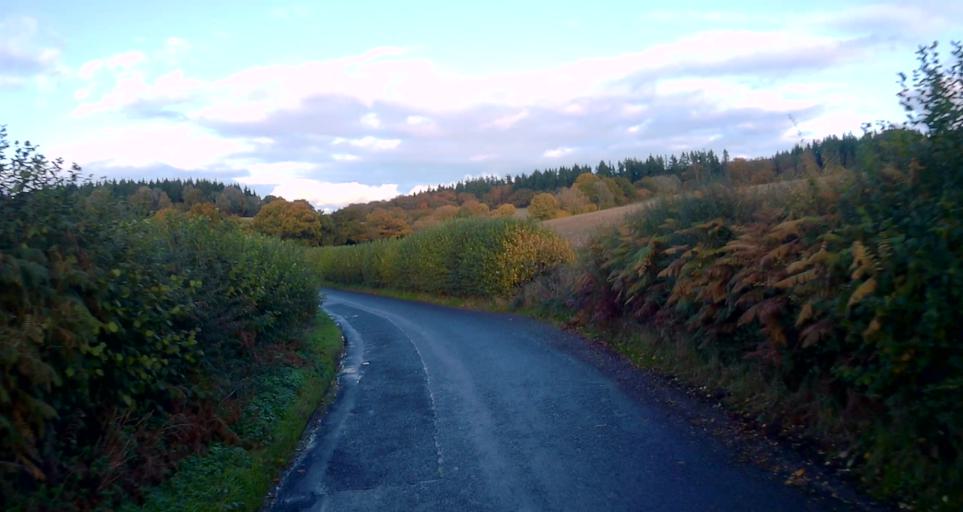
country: GB
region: England
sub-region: Hampshire
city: Basingstoke
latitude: 51.1895
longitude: -1.0778
